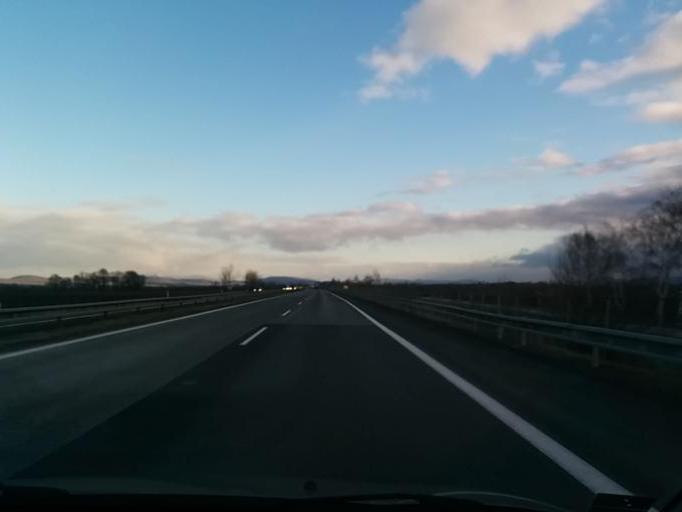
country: SK
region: Trnavsky
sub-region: Okres Trnava
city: Piestany
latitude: 48.5679
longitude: 17.7900
